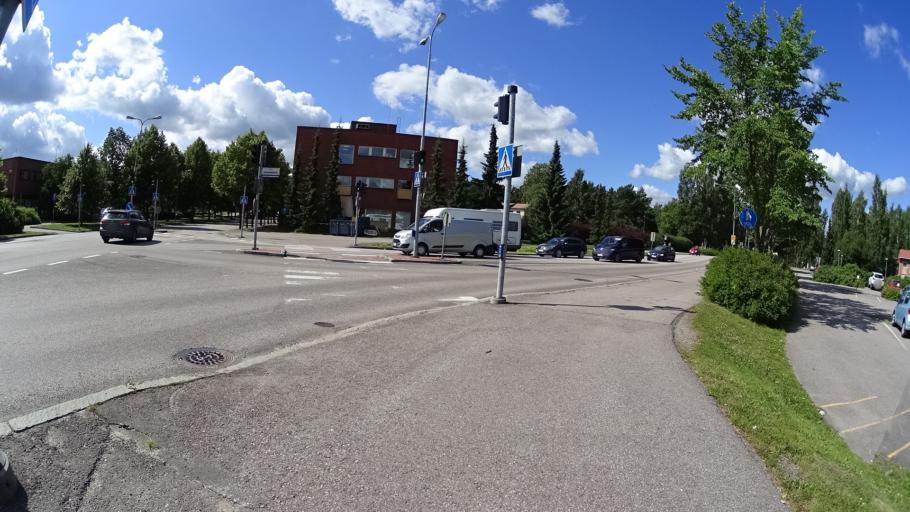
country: FI
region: Uusimaa
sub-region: Helsinki
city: Tuusula
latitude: 60.4033
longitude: 25.0257
